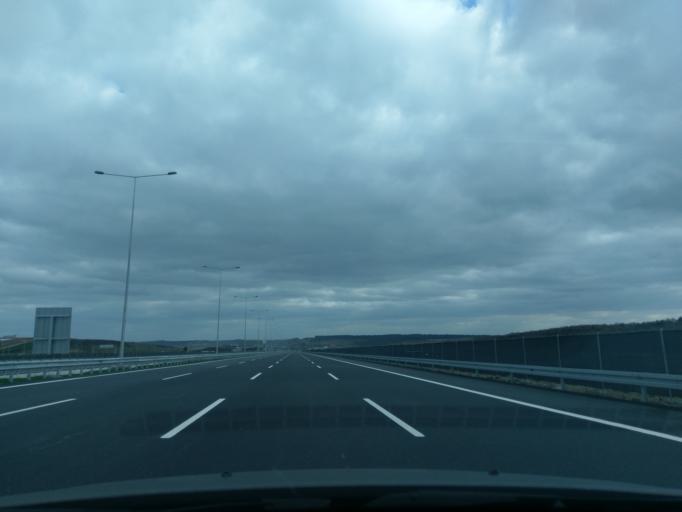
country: TR
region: Istanbul
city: Durusu
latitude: 41.2443
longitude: 28.7000
